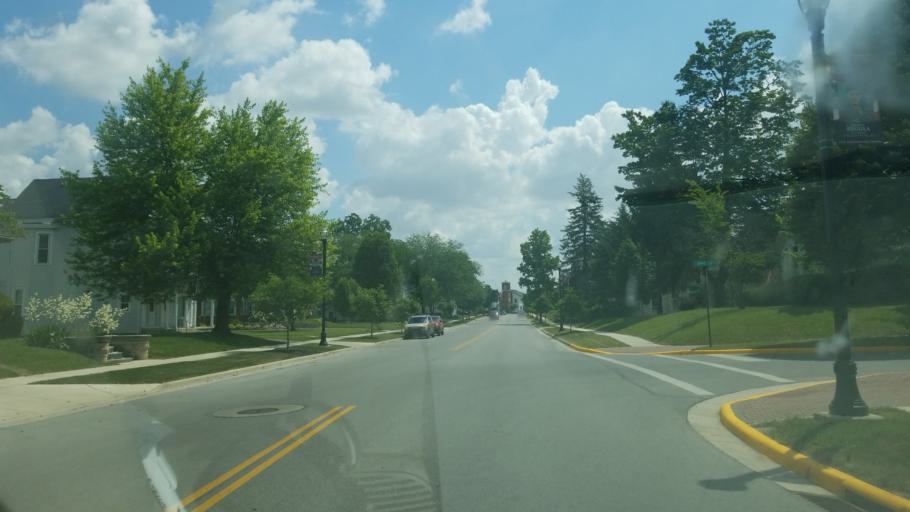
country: US
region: Ohio
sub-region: Auglaize County
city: Wapakoneta
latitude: 40.5700
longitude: -84.2006
